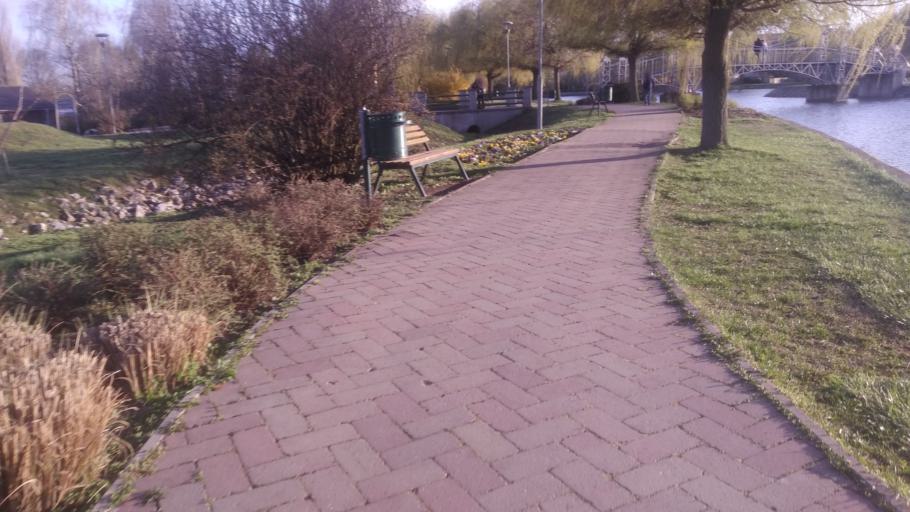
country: HU
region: Veszprem
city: Petfuerdo
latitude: 47.1637
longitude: 18.1248
